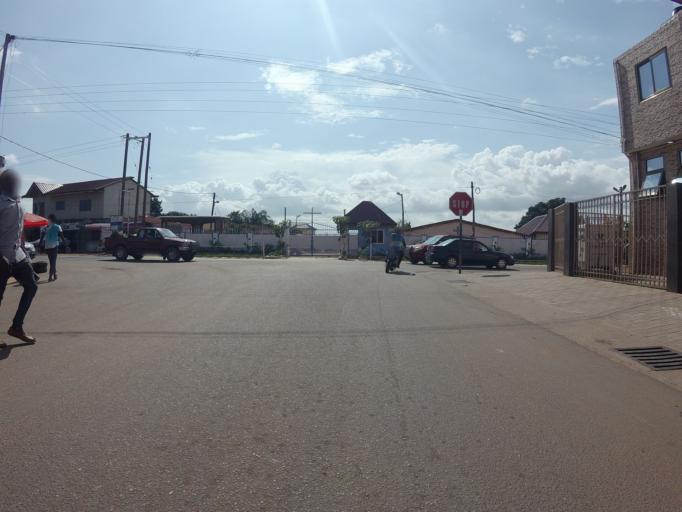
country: GH
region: Greater Accra
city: Medina Estates
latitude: 5.6791
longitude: -0.1807
